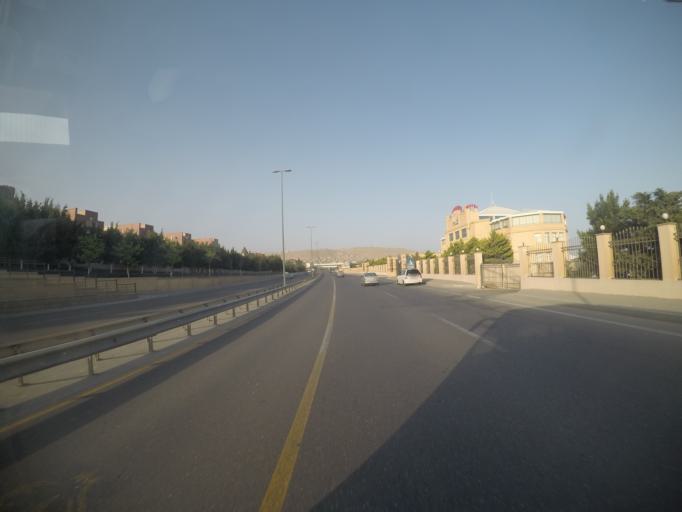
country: AZ
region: Baki
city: Badamdar
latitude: 40.3057
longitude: 49.7926
